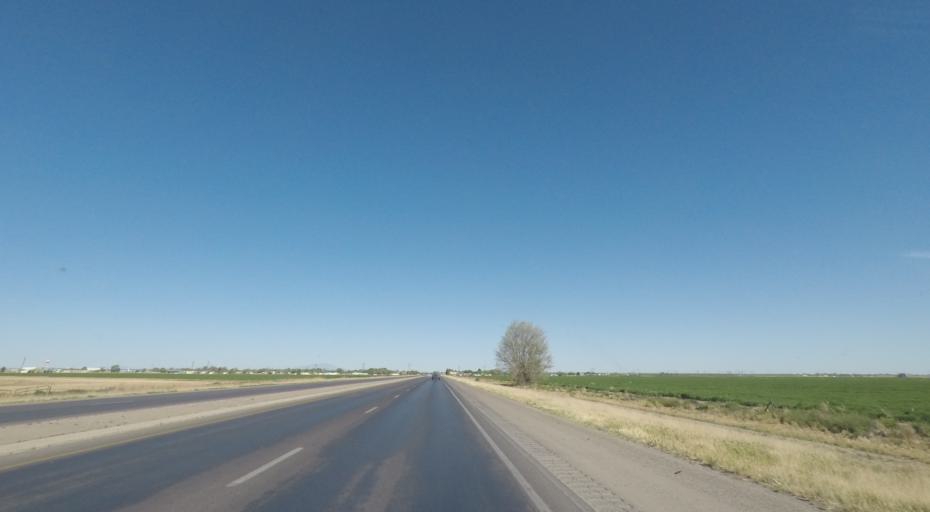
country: US
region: New Mexico
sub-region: Chaves County
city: Roswell
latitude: 33.3125
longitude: -104.4805
